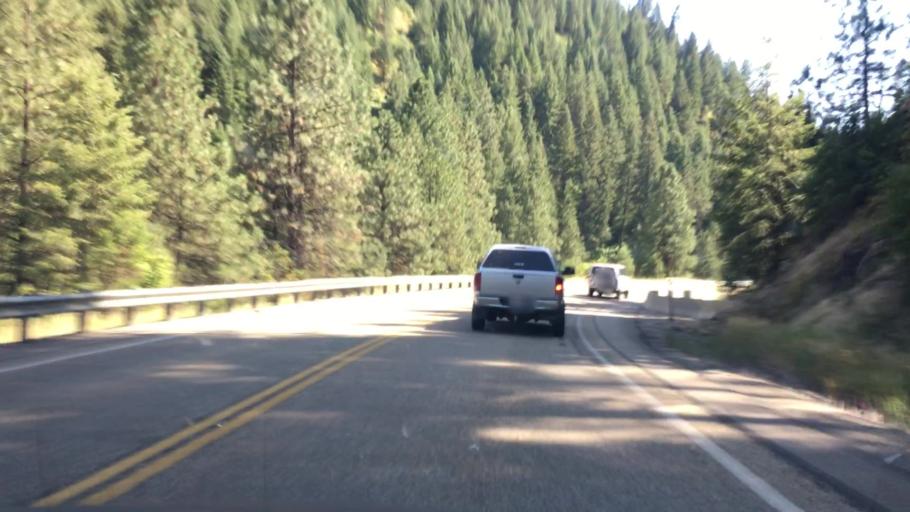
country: US
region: Idaho
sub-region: Valley County
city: Cascade
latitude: 44.1456
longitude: -116.1132
